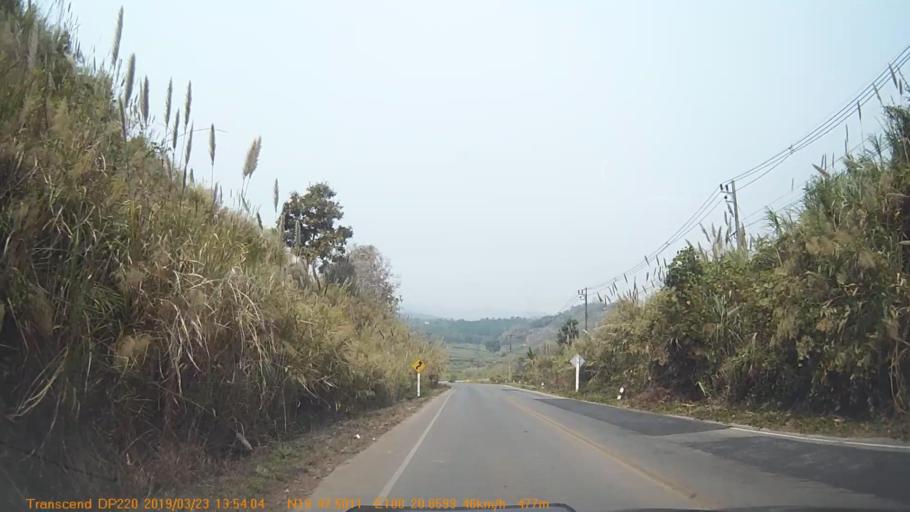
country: TH
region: Chiang Rai
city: Khun Tan
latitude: 19.7919
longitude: 100.3477
